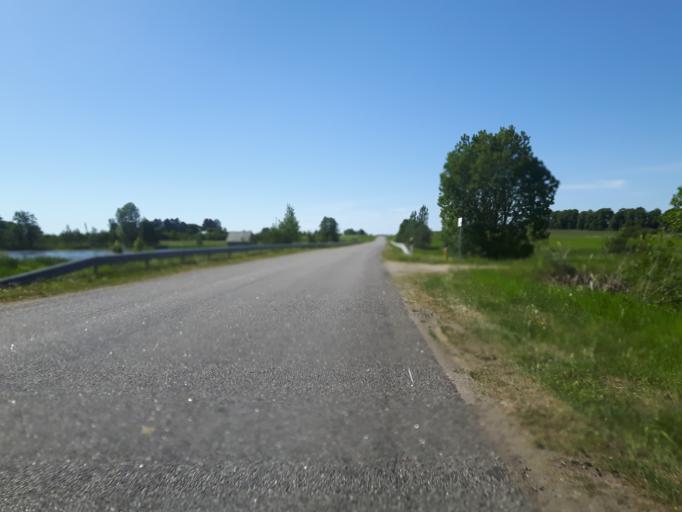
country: EE
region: Laeaene-Virumaa
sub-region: Haljala vald
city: Haljala
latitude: 59.5430
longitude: 26.1851
